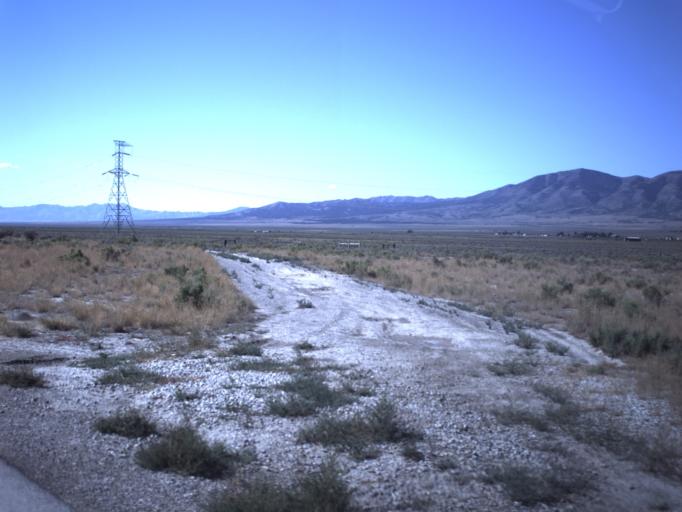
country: US
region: Utah
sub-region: Tooele County
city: Tooele
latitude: 40.3527
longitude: -112.4126
